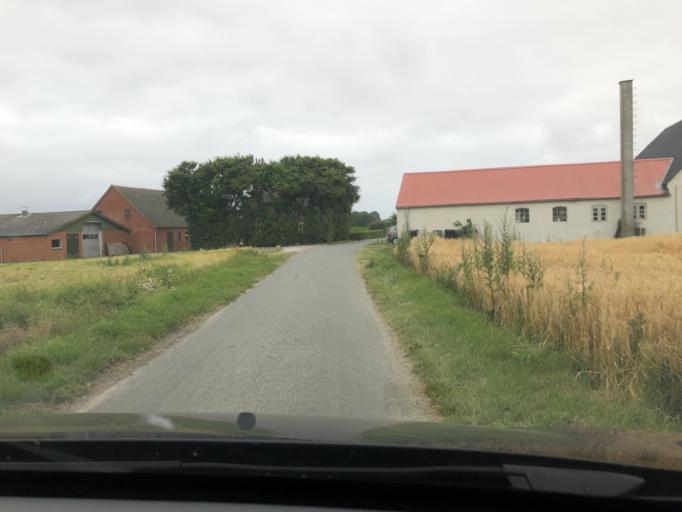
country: DK
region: South Denmark
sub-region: AEro Kommune
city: AEroskobing
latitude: 54.8406
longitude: 10.4269
